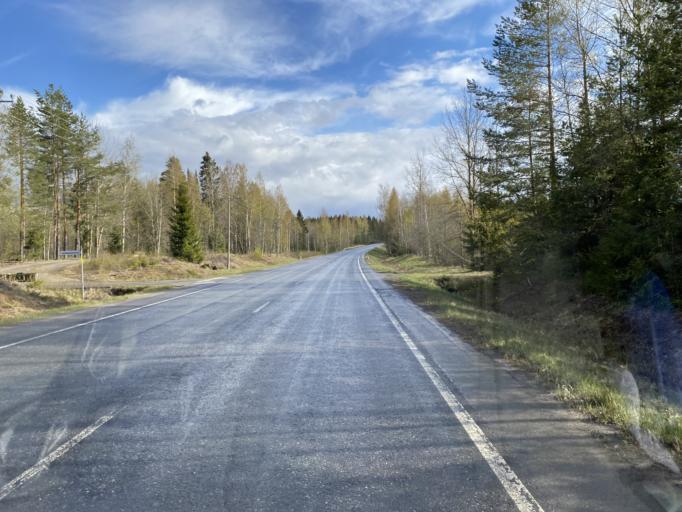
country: FI
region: Pirkanmaa
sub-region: Etelae-Pirkanmaa
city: Viiala
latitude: 61.2322
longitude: 23.7419
